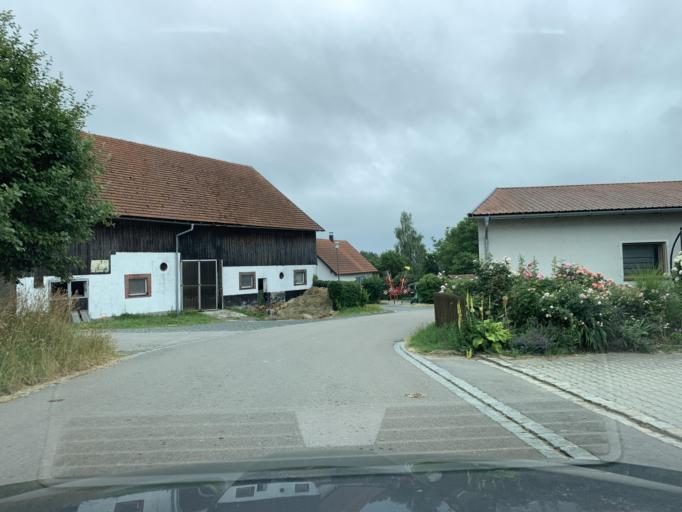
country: DE
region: Bavaria
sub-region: Upper Palatinate
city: Winklarn
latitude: 49.4138
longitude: 12.4516
